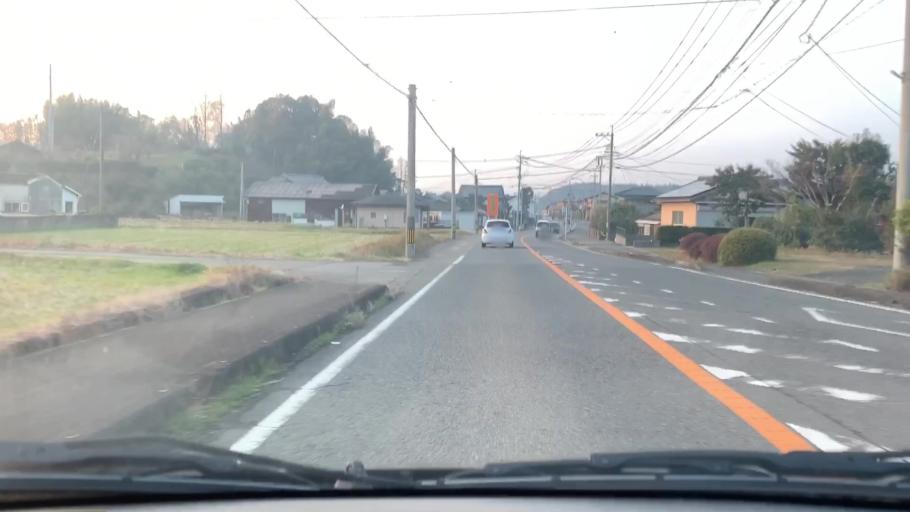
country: JP
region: Saga Prefecture
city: Imaricho-ko
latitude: 33.2662
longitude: 129.9020
